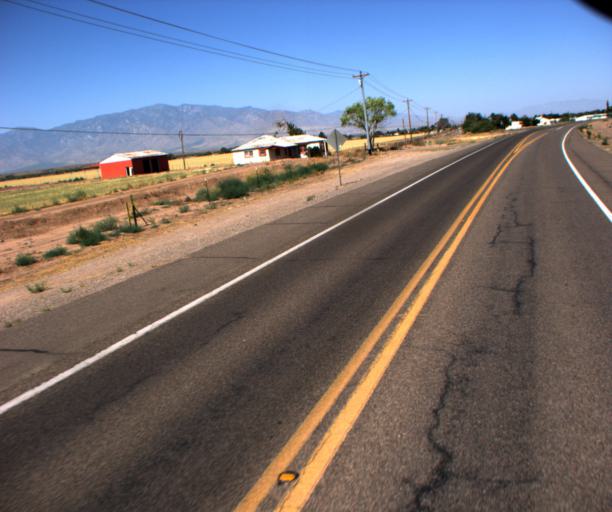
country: US
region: Arizona
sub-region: Graham County
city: Safford
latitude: 32.8129
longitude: -109.6168
